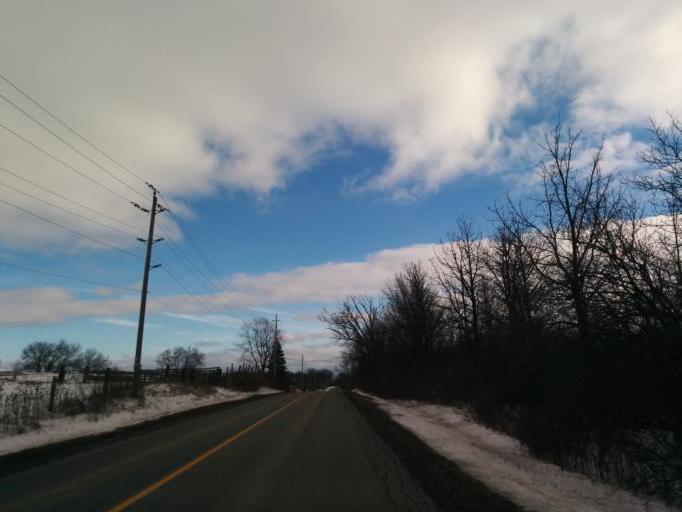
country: CA
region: Ontario
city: Ancaster
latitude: 42.9499
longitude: -79.8724
